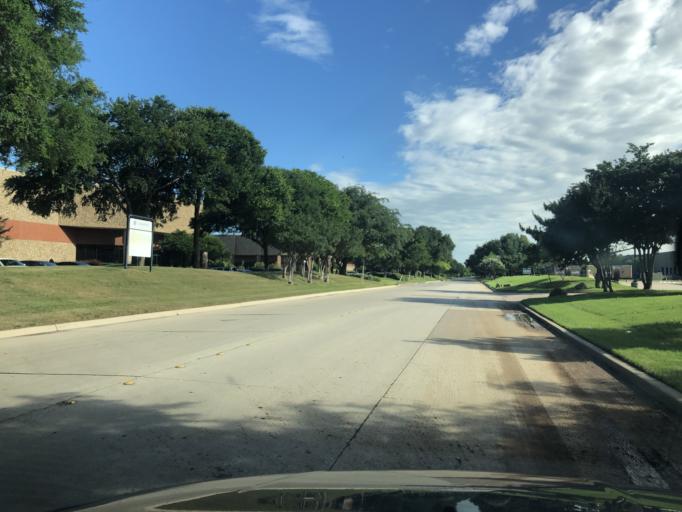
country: US
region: Texas
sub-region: Tarrant County
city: Euless
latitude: 32.8255
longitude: -97.0441
